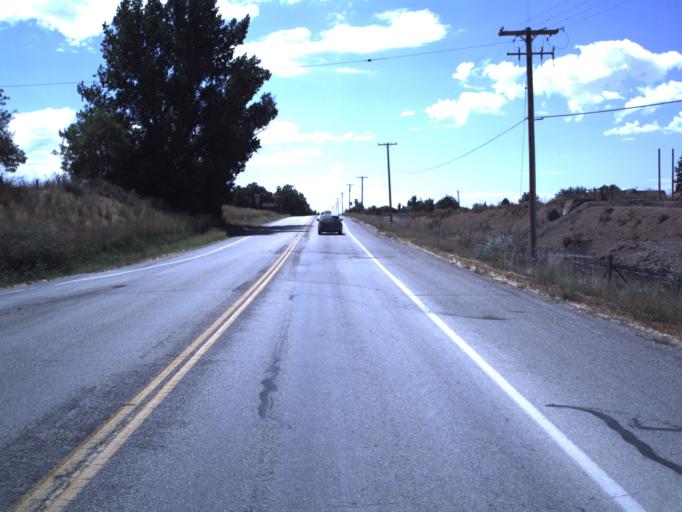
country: US
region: Utah
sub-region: Box Elder County
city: Garland
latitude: 41.7400
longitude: -112.1436
